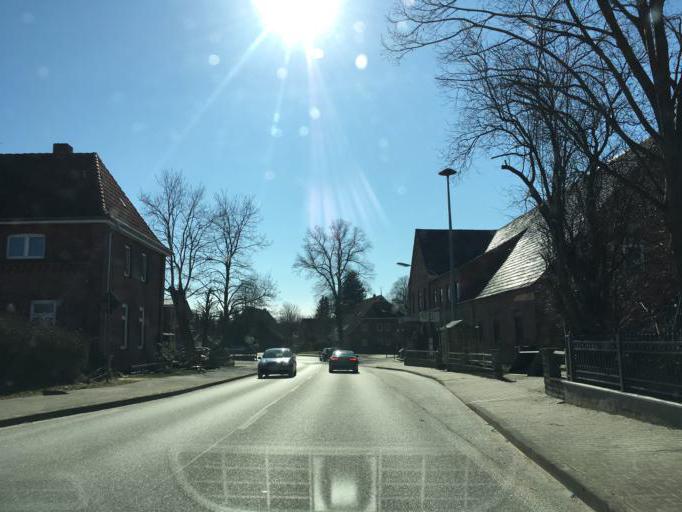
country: DE
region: Schleswig-Holstein
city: Berkenthin
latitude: 53.7318
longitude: 10.6502
